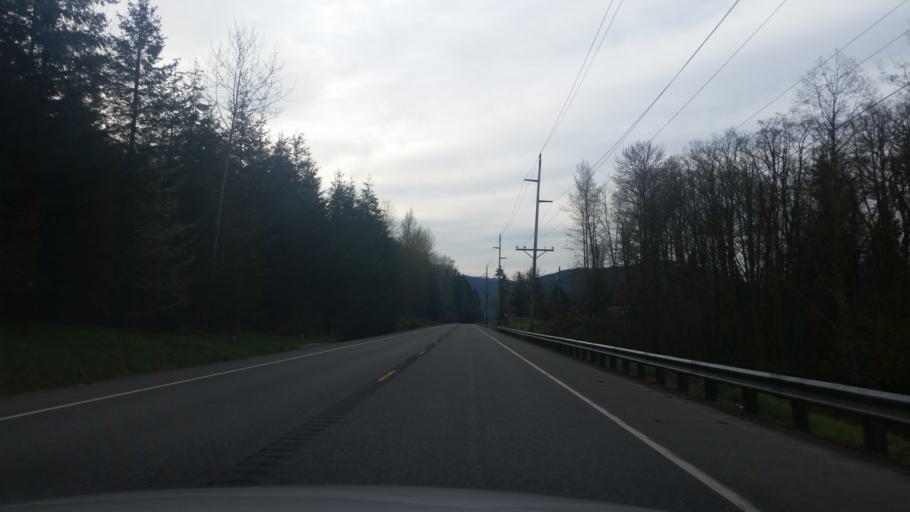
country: US
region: Washington
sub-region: Pierce County
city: Eatonville
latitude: 46.7759
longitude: -122.2227
